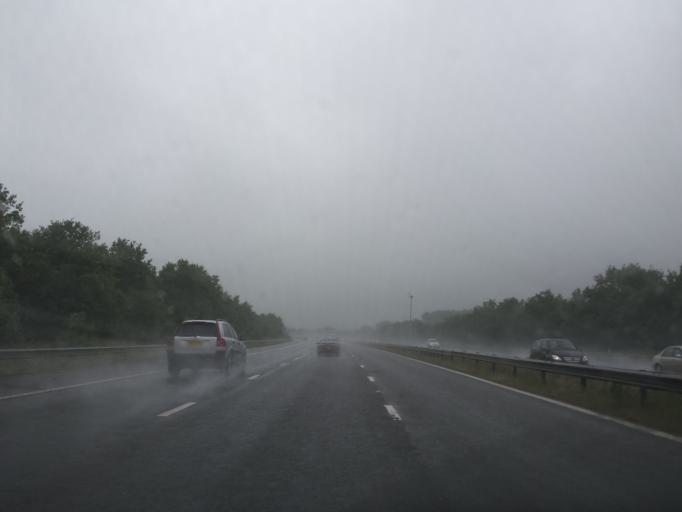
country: GB
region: England
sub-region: Leicestershire
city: Markfield
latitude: 52.6980
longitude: -1.2925
